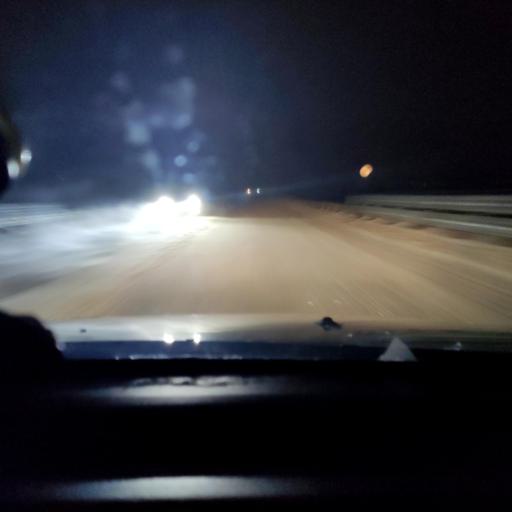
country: RU
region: Samara
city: Georgiyevka
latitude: 53.2719
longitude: 51.0429
